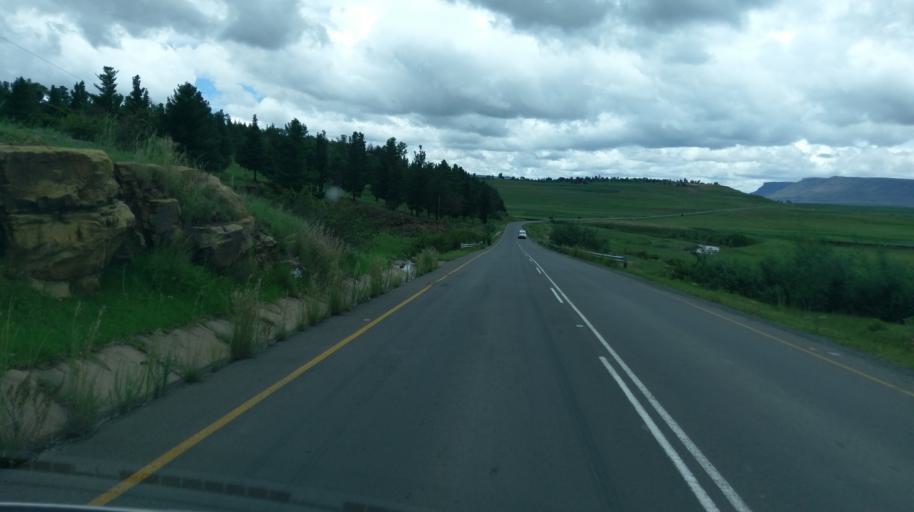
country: LS
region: Maseru
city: Maseru
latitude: -29.5181
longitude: 27.5239
